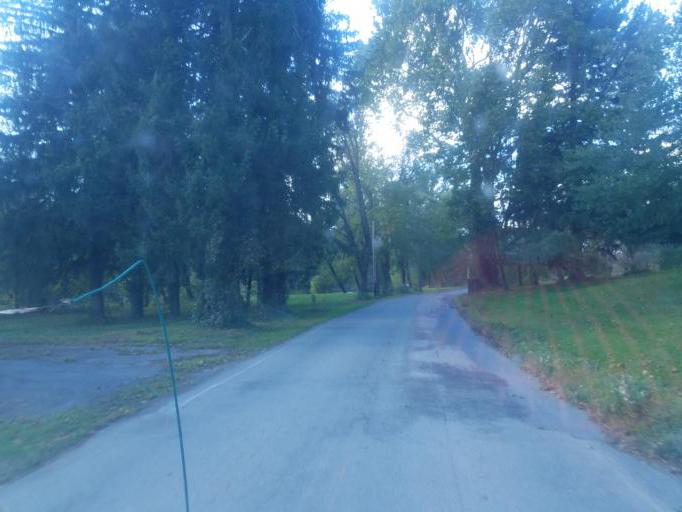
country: US
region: Pennsylvania
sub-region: Dauphin County
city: Middletown
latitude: 40.2059
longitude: -76.7128
